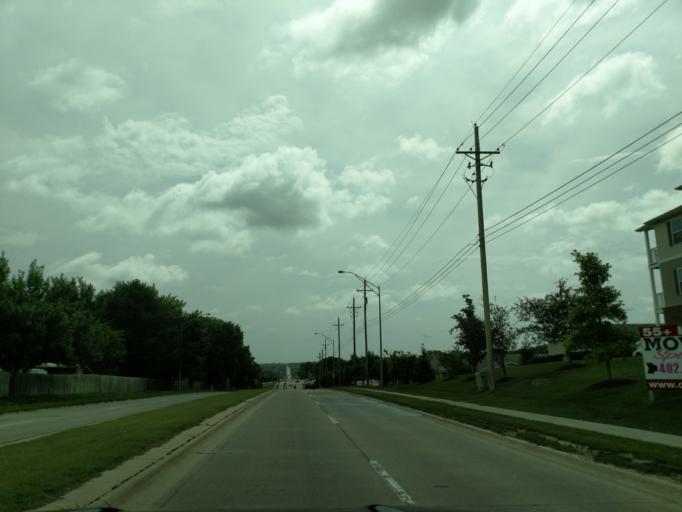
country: US
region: Nebraska
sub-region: Sarpy County
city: La Vista
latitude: 41.1908
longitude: -96.0303
